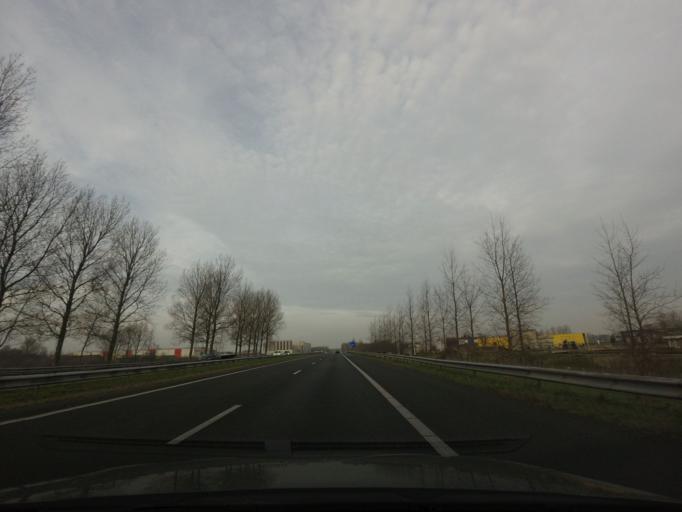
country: NL
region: North Holland
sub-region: Gemeente Medemblik
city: Opperdoes
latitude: 52.8342
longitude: 5.0213
